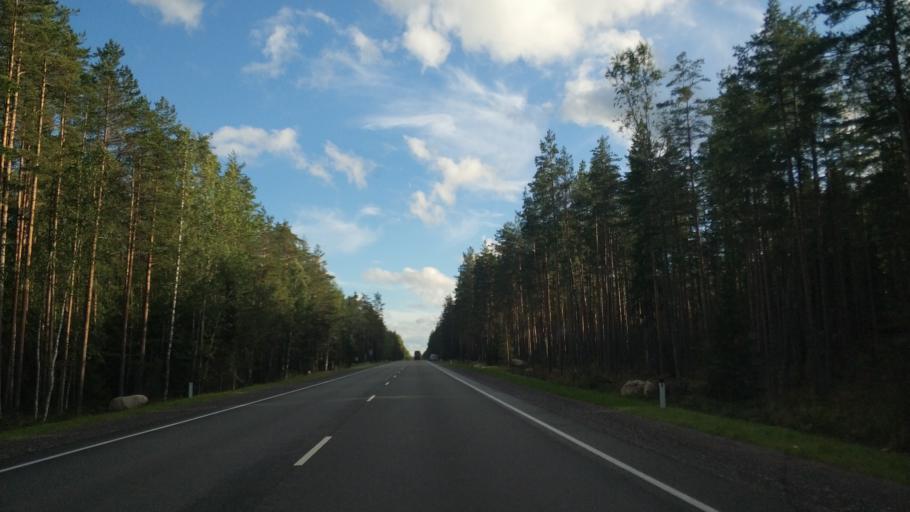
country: RU
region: Leningrad
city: Priozersk
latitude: 60.9040
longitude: 30.1602
